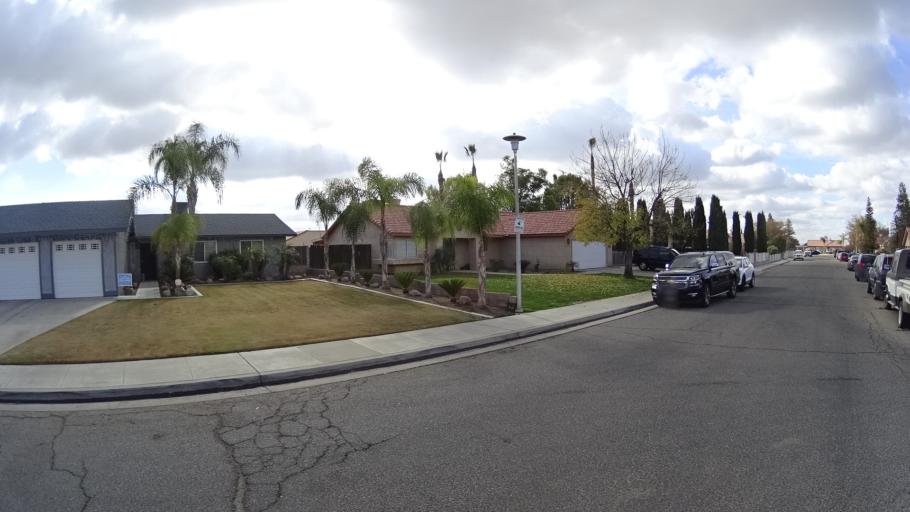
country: US
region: California
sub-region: Kern County
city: Bakersfield
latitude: 35.3562
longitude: -118.9521
